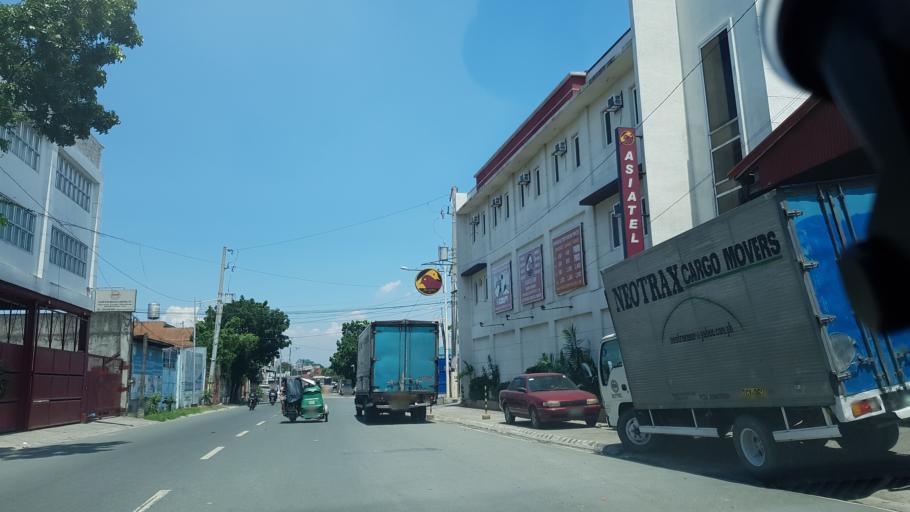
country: PH
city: Sambayanihan People's Village
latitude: 14.4691
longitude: 120.9969
